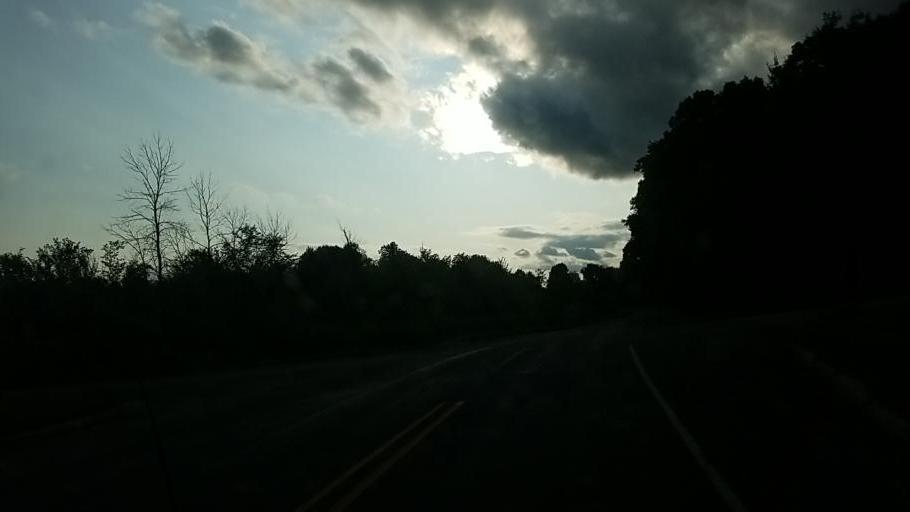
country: US
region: Michigan
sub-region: Montcalm County
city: Howard City
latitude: 43.3089
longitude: -85.3729
